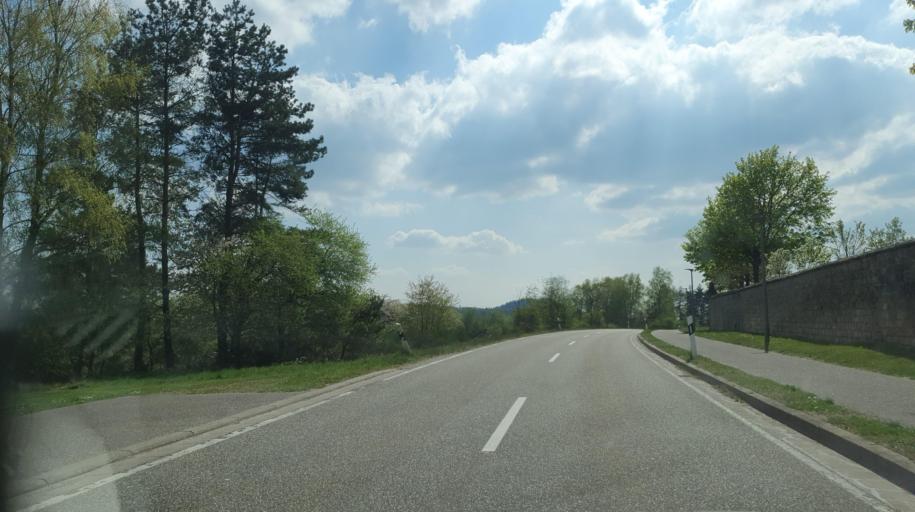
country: DE
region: Rheinland-Pfalz
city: Leimen
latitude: 49.2783
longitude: 7.7786
